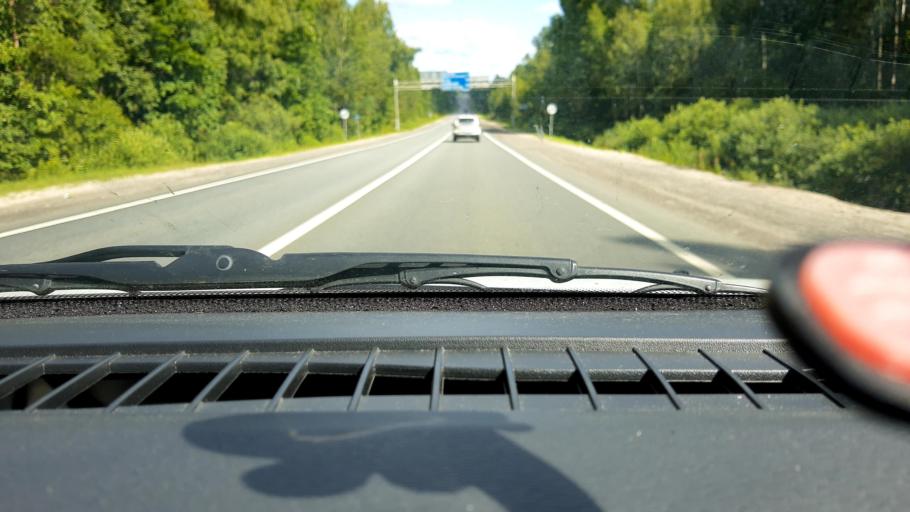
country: RU
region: Nizjnij Novgorod
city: Arzamas
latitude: 55.4677
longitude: 43.8795
